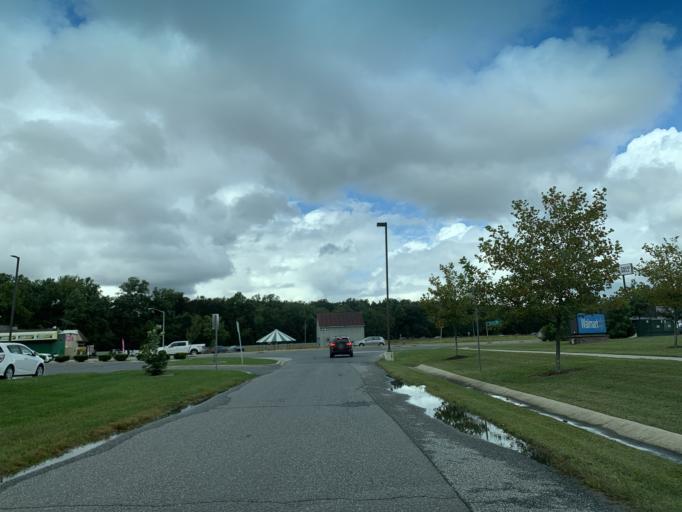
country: US
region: Maryland
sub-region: Caroline County
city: Denton
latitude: 38.8754
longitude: -75.8229
